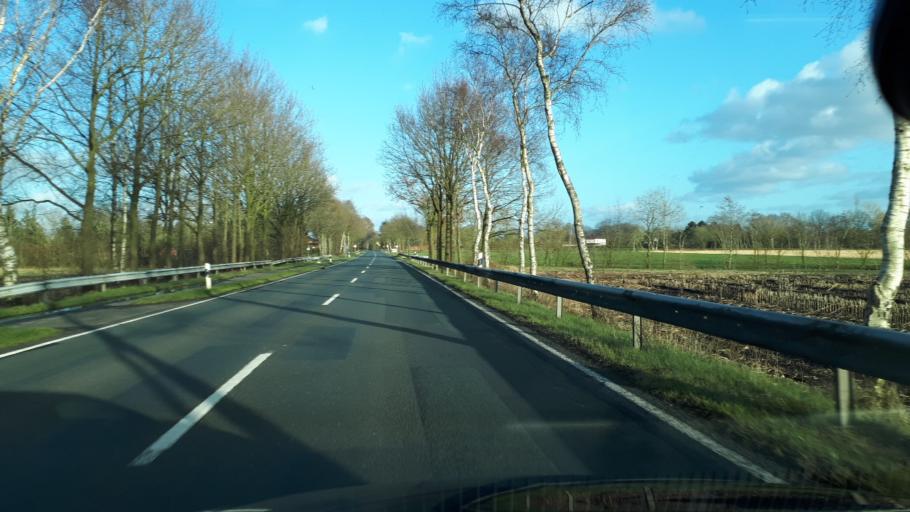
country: DE
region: Lower Saxony
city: Molbergen
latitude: 52.8671
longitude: 7.9033
